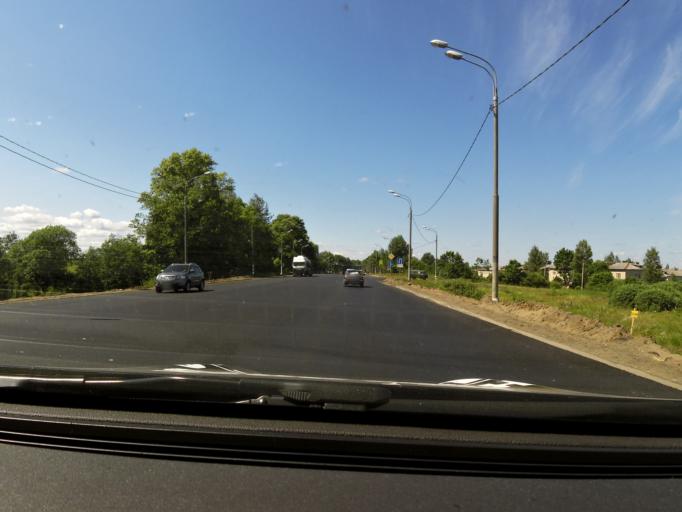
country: RU
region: Novgorod
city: Valday
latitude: 57.9534
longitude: 33.2722
